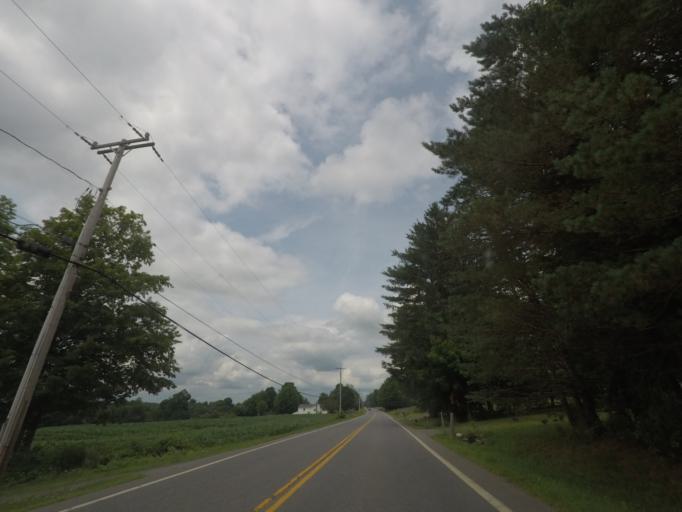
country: US
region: New York
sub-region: Saratoga County
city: Stillwater
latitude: 43.0144
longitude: -73.6931
